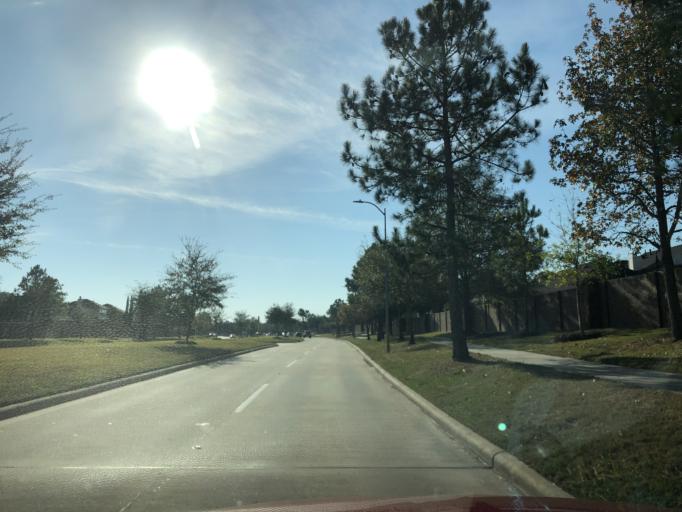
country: US
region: Texas
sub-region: Harris County
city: Tomball
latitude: 30.0522
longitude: -95.5679
